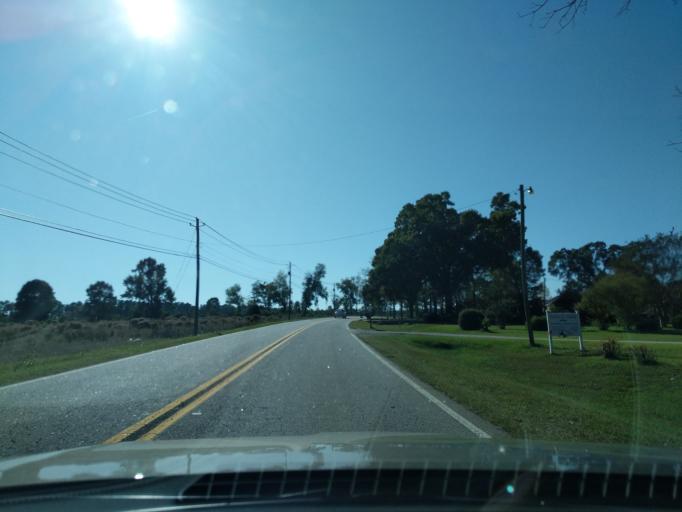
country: US
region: Georgia
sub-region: Columbia County
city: Grovetown
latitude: 33.4674
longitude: -82.1596
